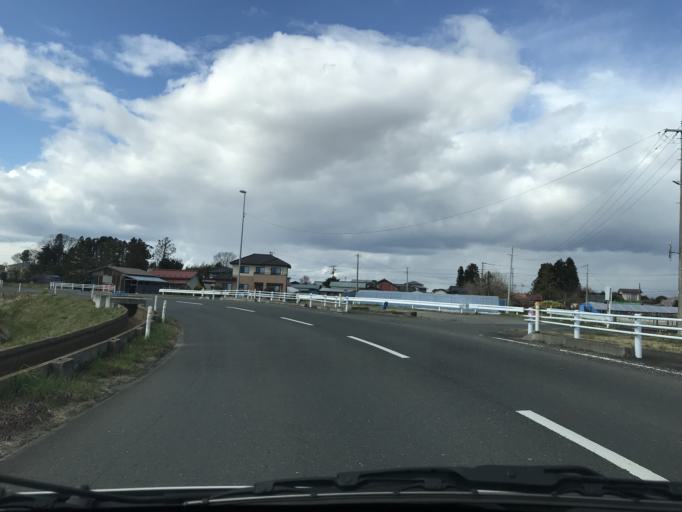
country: JP
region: Miyagi
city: Wakuya
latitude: 38.6551
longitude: 141.2052
